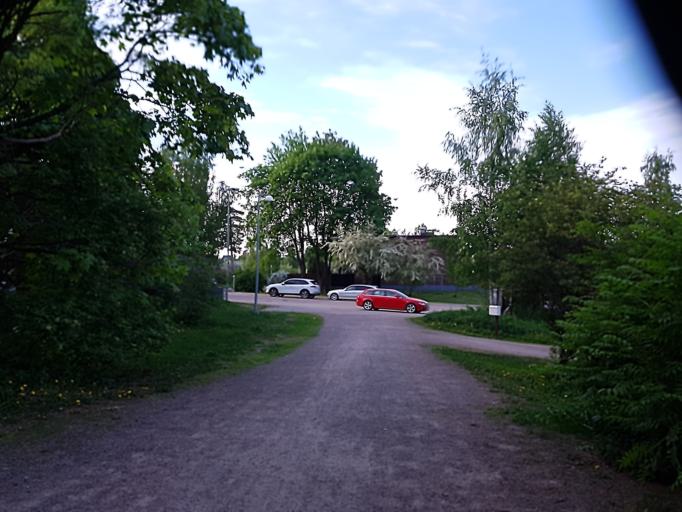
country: FI
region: Uusimaa
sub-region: Helsinki
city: Helsinki
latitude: 60.2365
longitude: 24.9386
